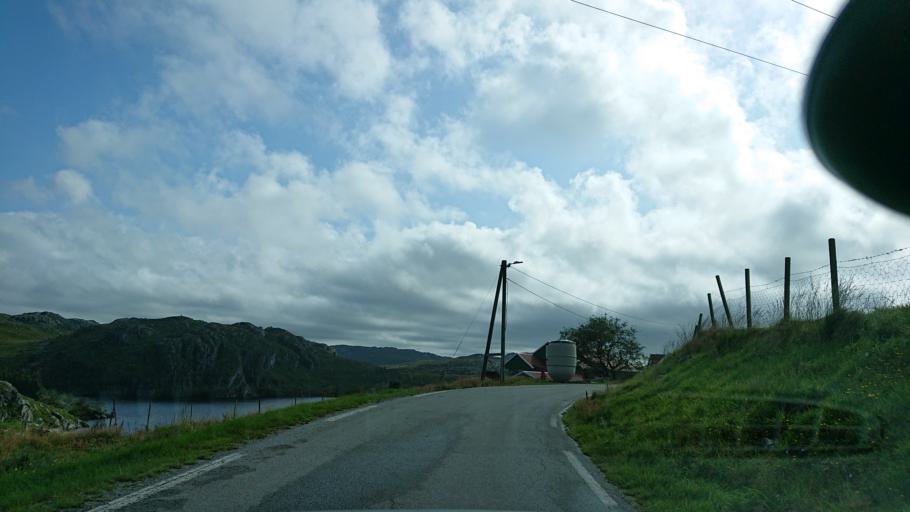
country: NO
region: Rogaland
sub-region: Gjesdal
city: Algard
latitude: 58.6980
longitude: 5.8890
